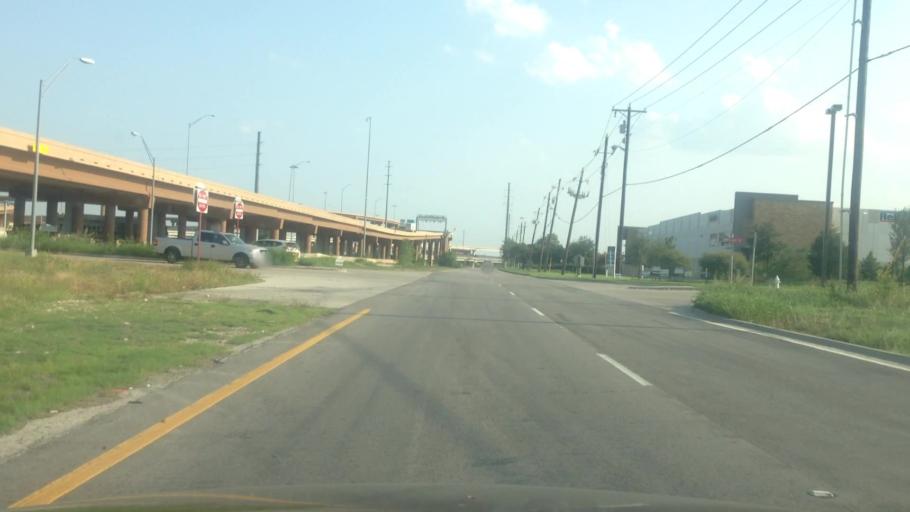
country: US
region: Texas
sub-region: Dallas County
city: Farmers Branch
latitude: 32.9148
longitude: -96.9000
